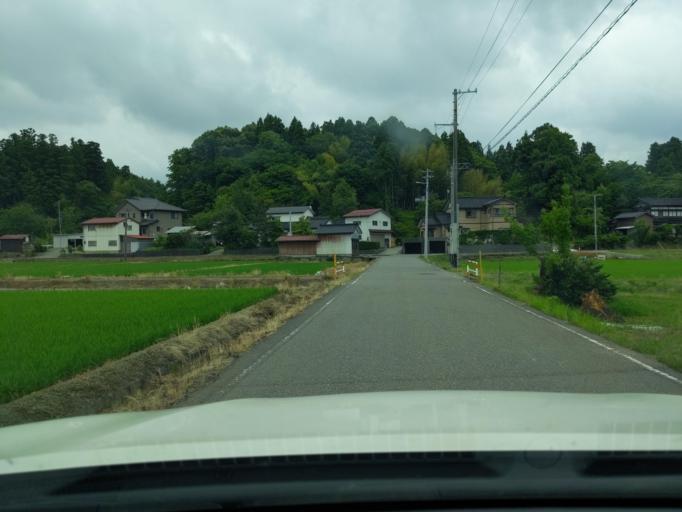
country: JP
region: Niigata
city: Kashiwazaki
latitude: 37.3427
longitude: 138.5884
